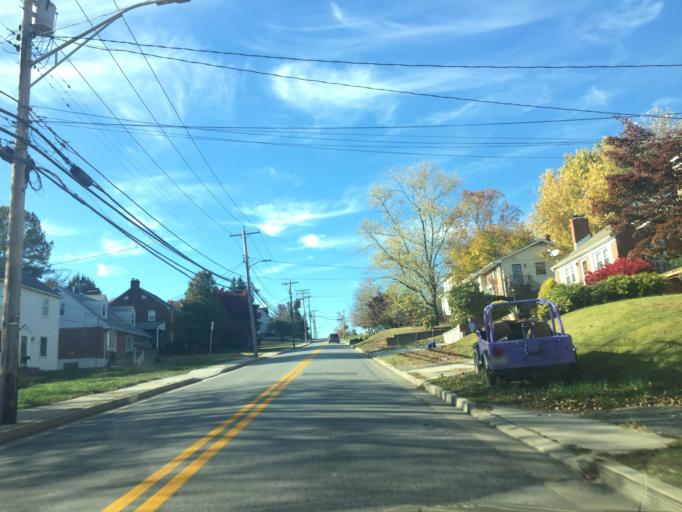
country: US
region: Maryland
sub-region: Baltimore County
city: Overlea
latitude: 39.3616
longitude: -76.5251
